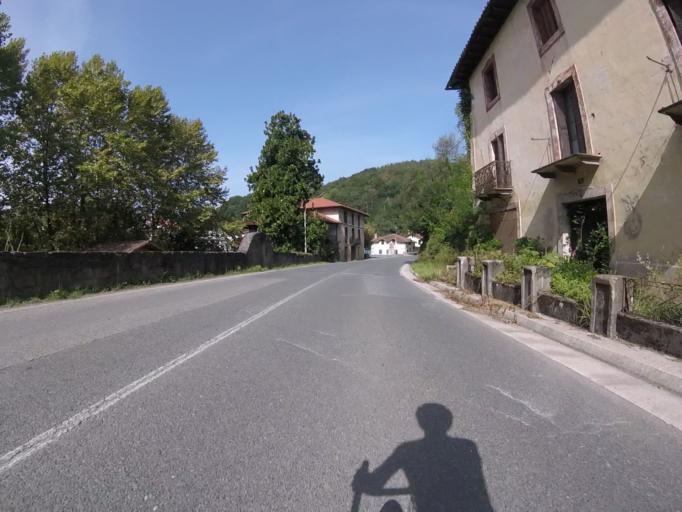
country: ES
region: Navarre
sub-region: Provincia de Navarra
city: Doneztebe
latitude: 43.1343
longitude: -1.6638
